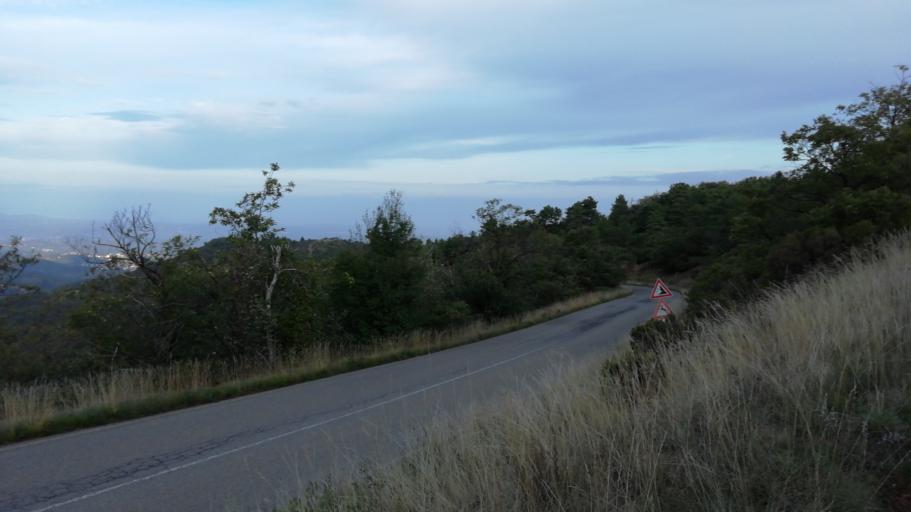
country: IT
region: Piedmont
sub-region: Provincia di Alessandria
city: Bosio
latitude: 44.6229
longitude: 8.7905
